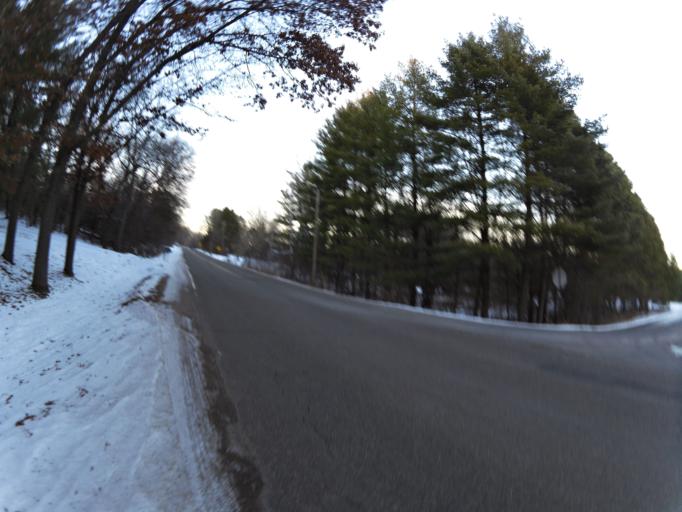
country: US
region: Minnesota
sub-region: Washington County
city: Lake Elmo
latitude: 44.9758
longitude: -92.8379
